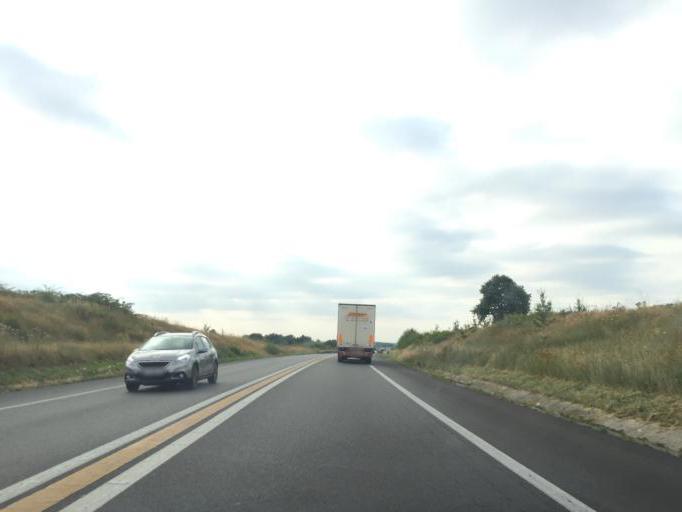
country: FR
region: Auvergne
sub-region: Departement de l'Allier
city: Diou
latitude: 46.5183
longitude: 3.7390
